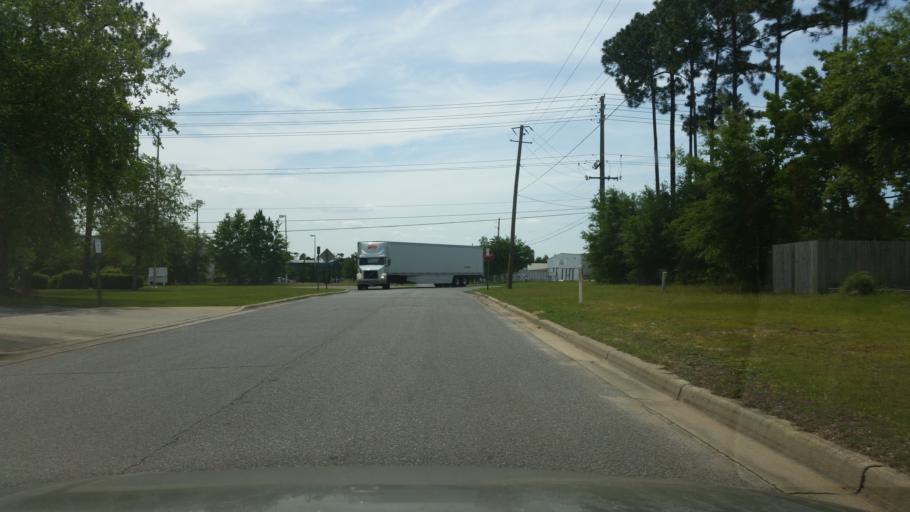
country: US
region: Florida
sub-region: Escambia County
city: Ferry Pass
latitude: 30.5200
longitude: -87.1893
